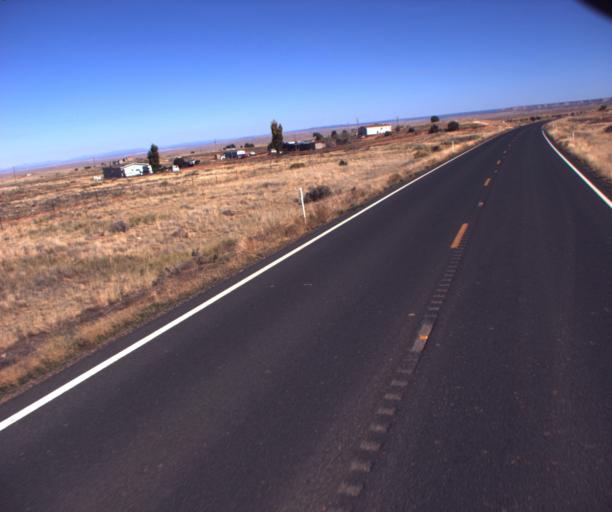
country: US
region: Arizona
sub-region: Apache County
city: Ganado
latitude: 35.7830
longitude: -109.7171
